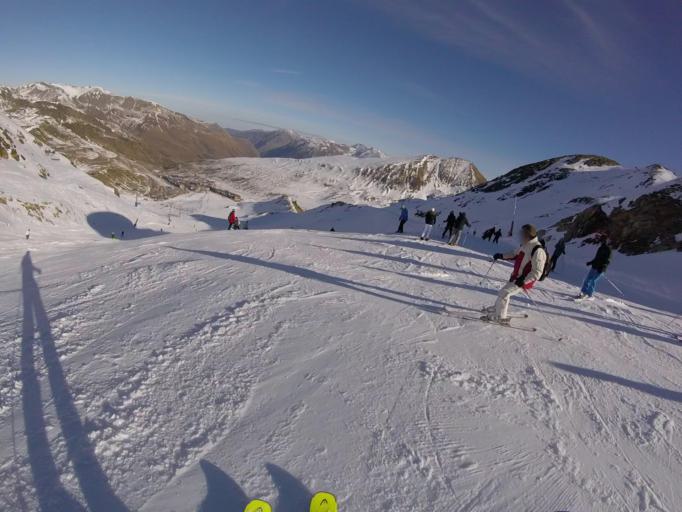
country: AD
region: Encamp
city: Pas de la Casa
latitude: 42.5281
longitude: 1.7208
